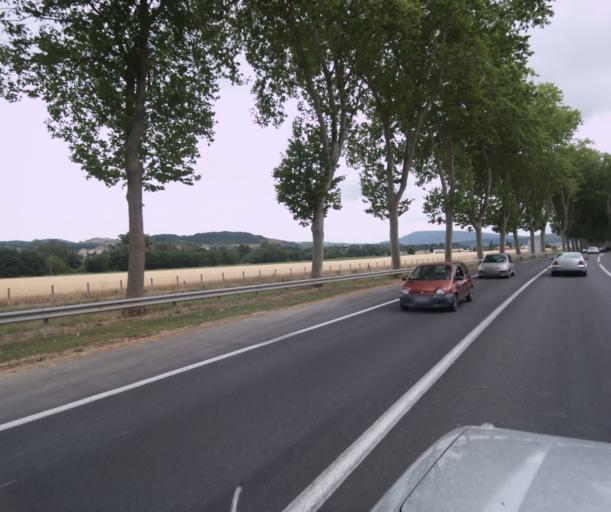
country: FR
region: Languedoc-Roussillon
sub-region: Departement de l'Aude
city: Limoux
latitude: 43.0846
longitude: 2.2257
